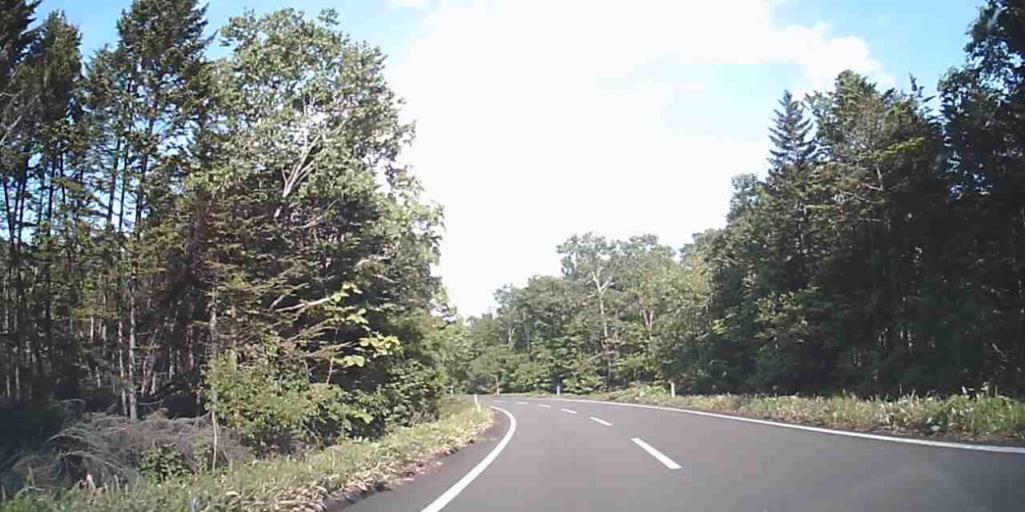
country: JP
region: Hokkaido
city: Shiraoi
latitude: 42.6809
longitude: 141.4454
